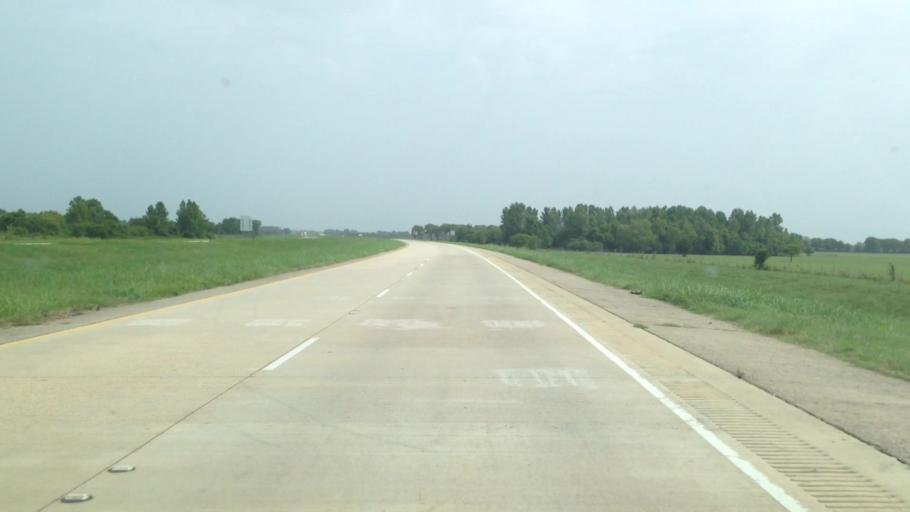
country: US
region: Louisiana
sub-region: Caddo Parish
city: Vivian
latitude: 32.8608
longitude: -93.8607
